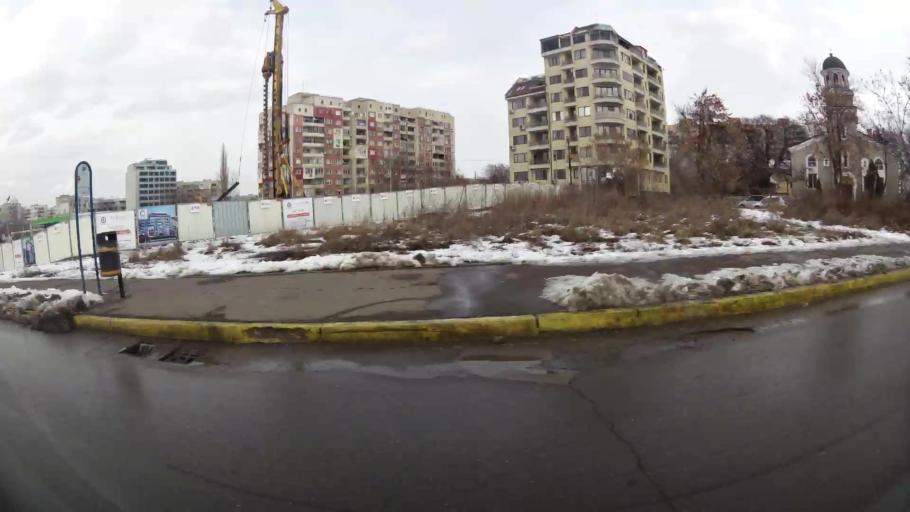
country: BG
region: Sofia-Capital
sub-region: Stolichna Obshtina
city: Sofia
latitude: 42.7007
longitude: 23.3515
